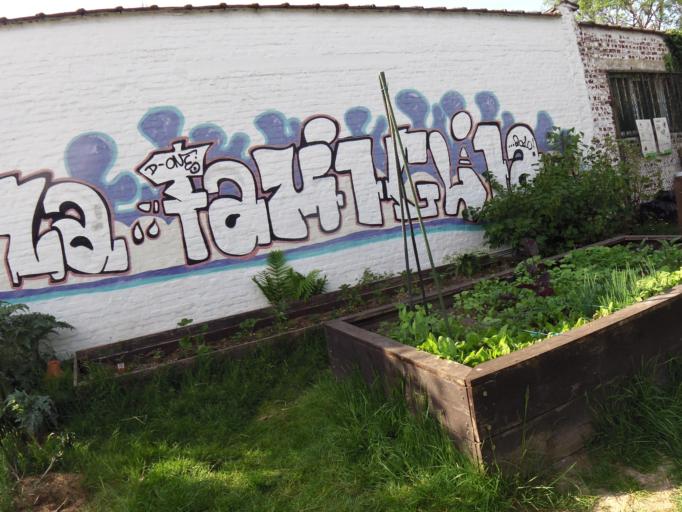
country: BE
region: Flanders
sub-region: Provincie Vlaams-Brabant
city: Diegem
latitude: 50.8455
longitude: 4.4134
